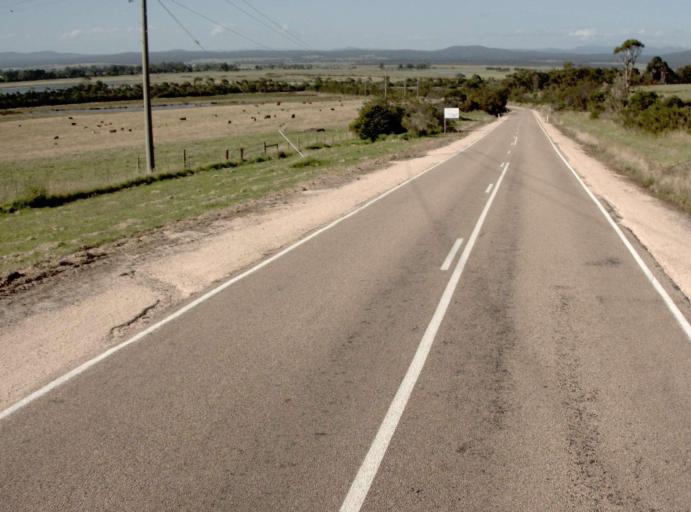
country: AU
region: Victoria
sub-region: East Gippsland
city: Lakes Entrance
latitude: -37.7858
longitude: 148.5379
